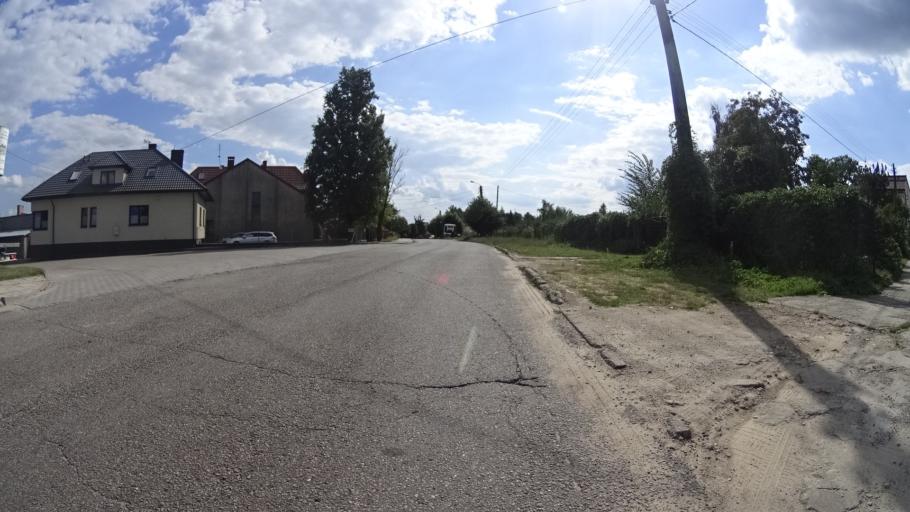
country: PL
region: Masovian Voivodeship
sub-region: Powiat grojecki
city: Mogielnica
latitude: 51.6861
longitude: 20.7182
